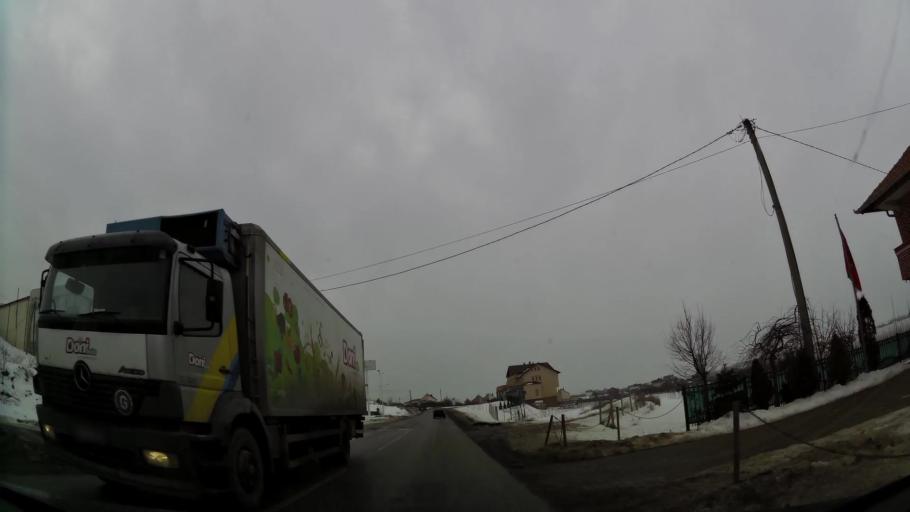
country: XK
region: Pristina
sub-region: Komuna e Prishtines
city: Pristina
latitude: 42.7261
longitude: 21.1445
